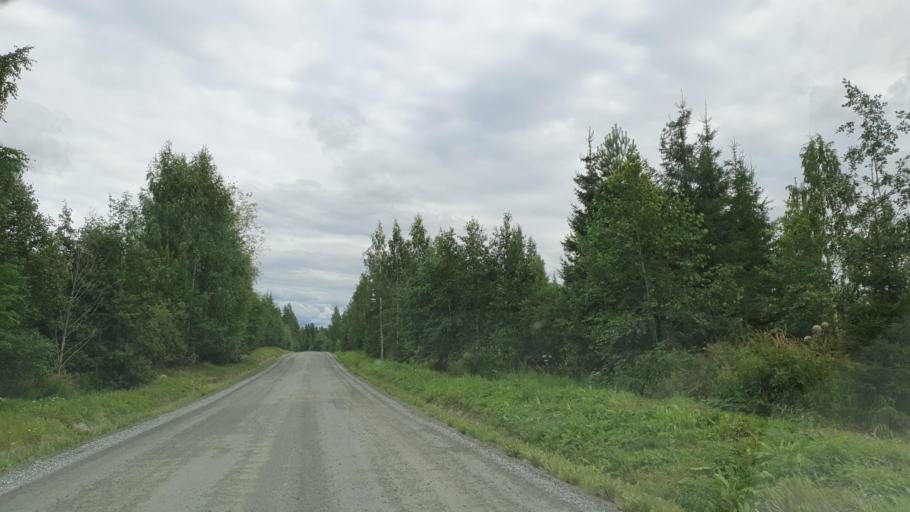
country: FI
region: Northern Savo
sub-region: Ylae-Savo
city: Iisalmi
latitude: 63.5181
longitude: 27.1030
